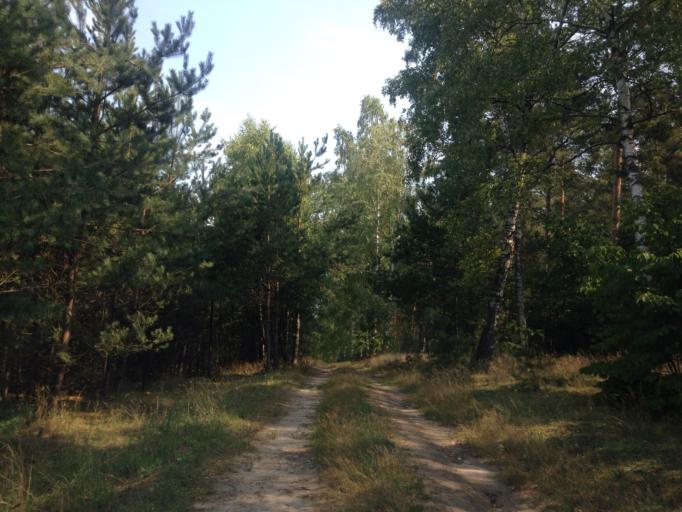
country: PL
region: Kujawsko-Pomorskie
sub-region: Powiat golubsko-dobrzynski
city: Golub-Dobrzyn
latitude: 53.1372
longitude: 19.0965
